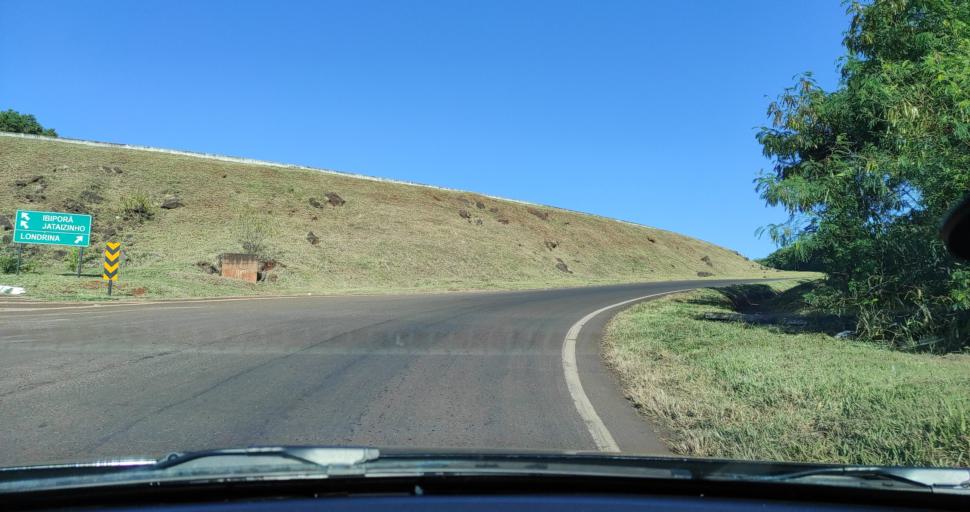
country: BR
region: Parana
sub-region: Ibipora
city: Ibipora
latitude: -23.2493
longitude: -51.0471
